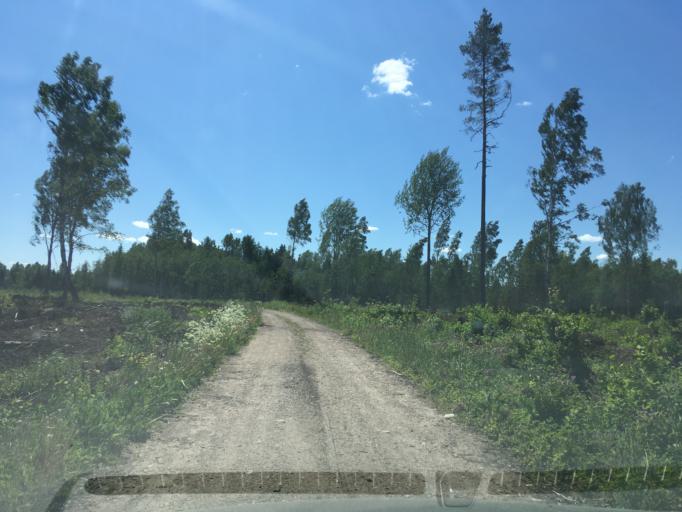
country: EE
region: Harju
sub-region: Raasiku vald
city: Raasiku
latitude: 59.1556
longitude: 25.1440
